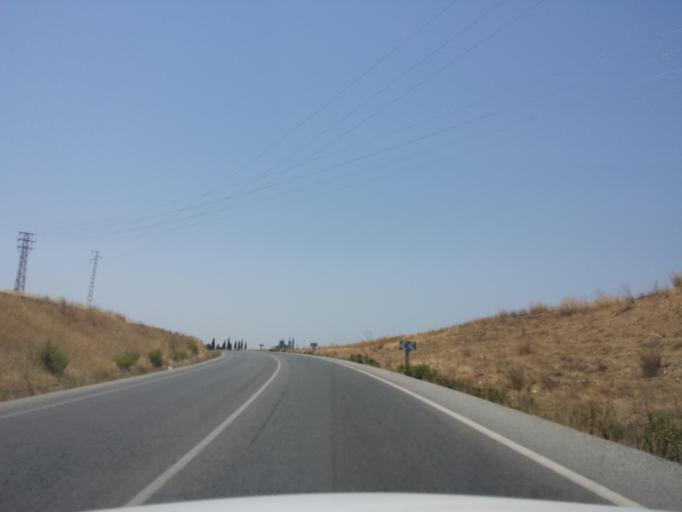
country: ES
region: Andalusia
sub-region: Provincia de Sevilla
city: Acala del Rio
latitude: 37.5284
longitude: -5.9721
